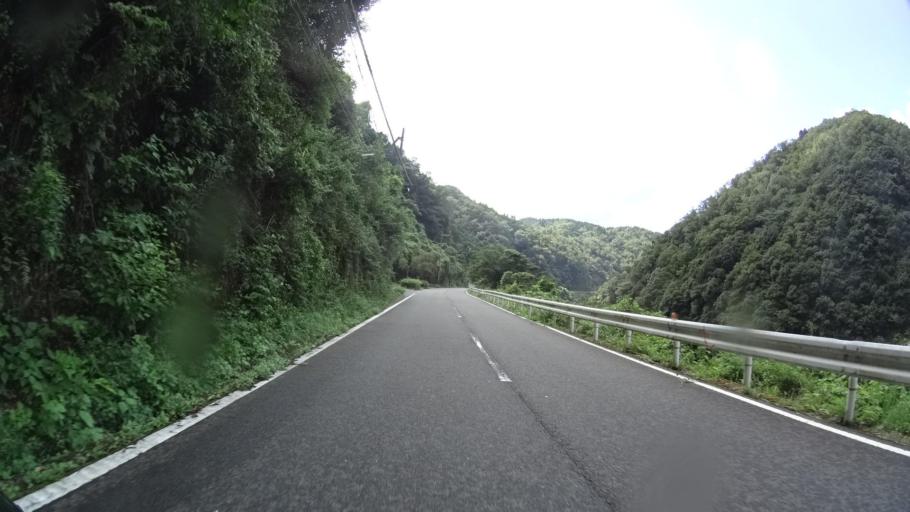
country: JP
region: Mie
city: Ueno-ebisumachi
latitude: 34.7655
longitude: 136.0013
